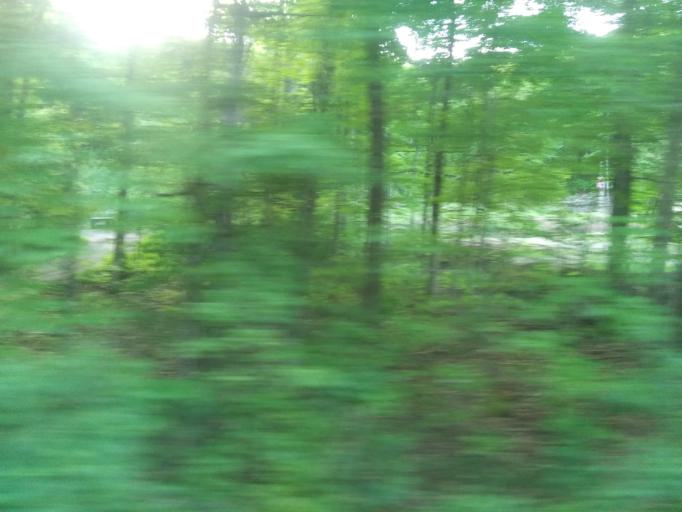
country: US
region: Massachusetts
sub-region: Franklin County
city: Buckland
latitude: 42.5783
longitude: -72.7727
